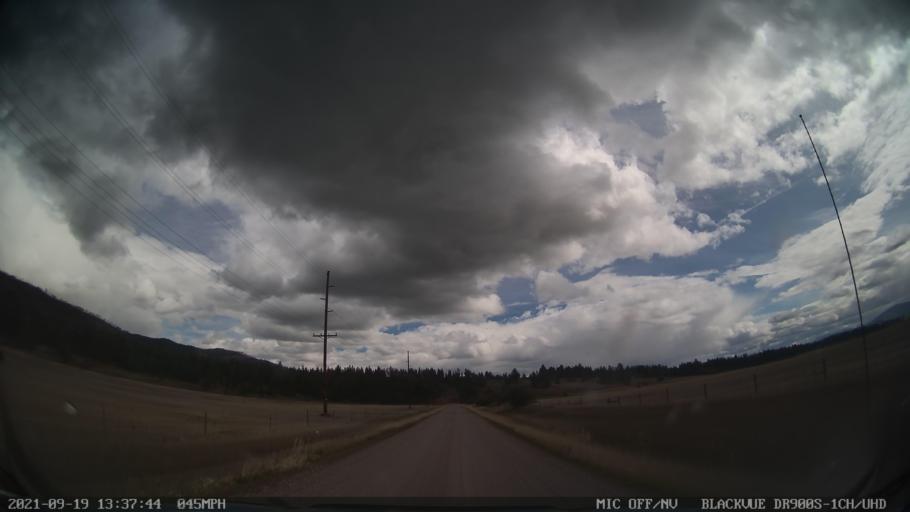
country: US
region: Montana
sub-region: Missoula County
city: Seeley Lake
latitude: 47.1066
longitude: -113.2786
